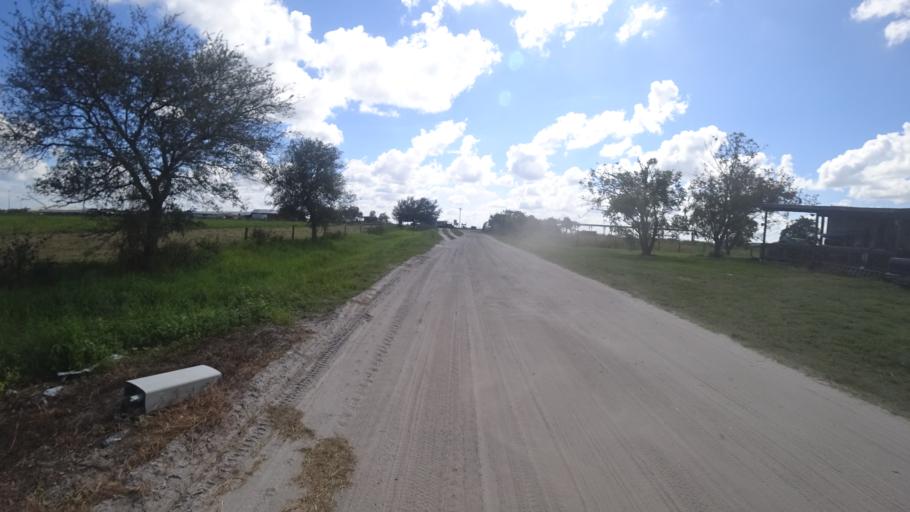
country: US
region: Florida
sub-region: Sarasota County
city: Warm Mineral Springs
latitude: 27.3157
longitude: -82.1304
